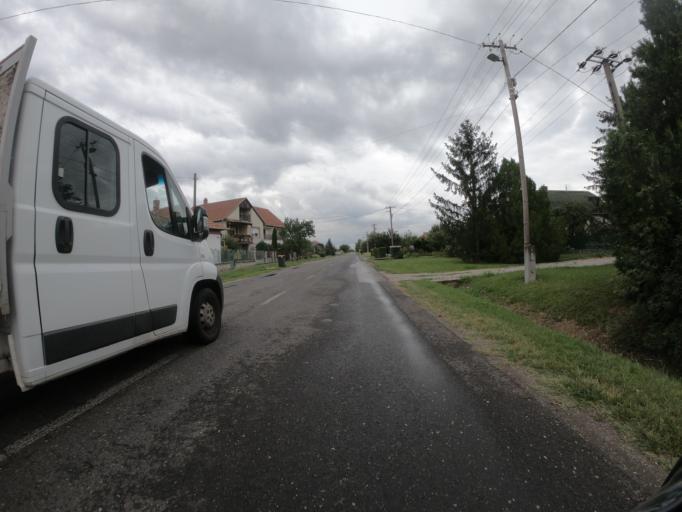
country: HU
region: Borsod-Abauj-Zemplen
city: Mezokovesd
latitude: 47.8051
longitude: 20.5918
